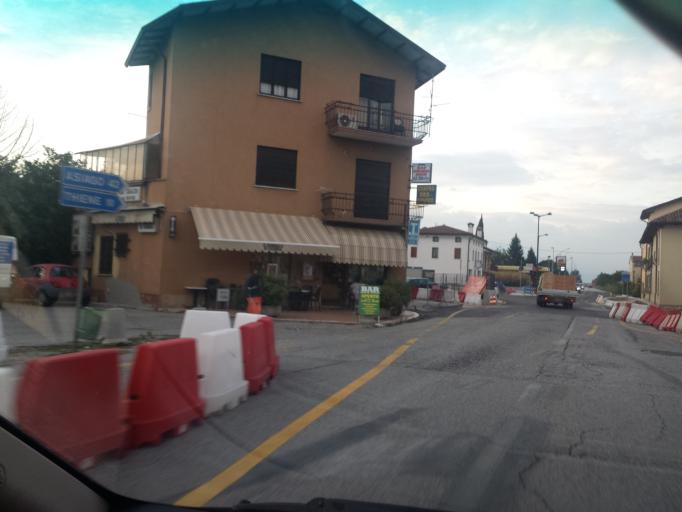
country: IT
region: Veneto
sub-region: Provincia di Vicenza
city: Motta
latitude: 45.6039
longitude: 11.4936
